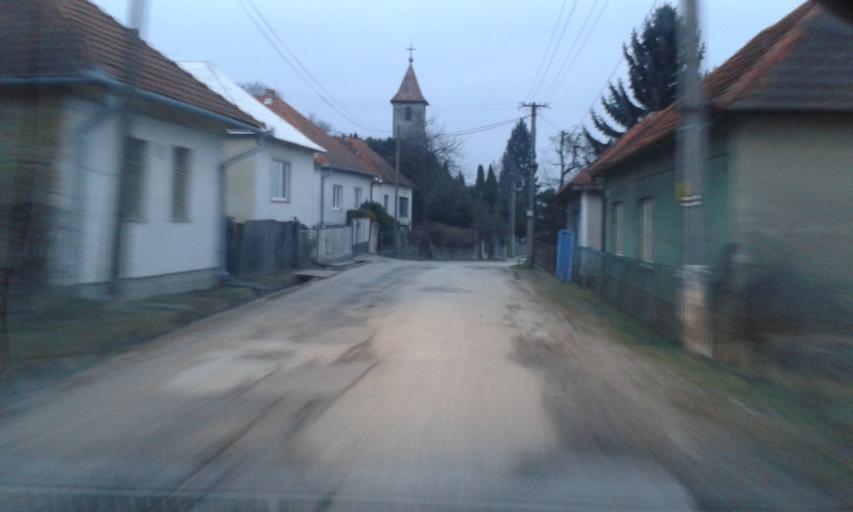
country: SK
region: Nitriansky
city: Zlate Moravce
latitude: 48.4636
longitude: 18.3142
